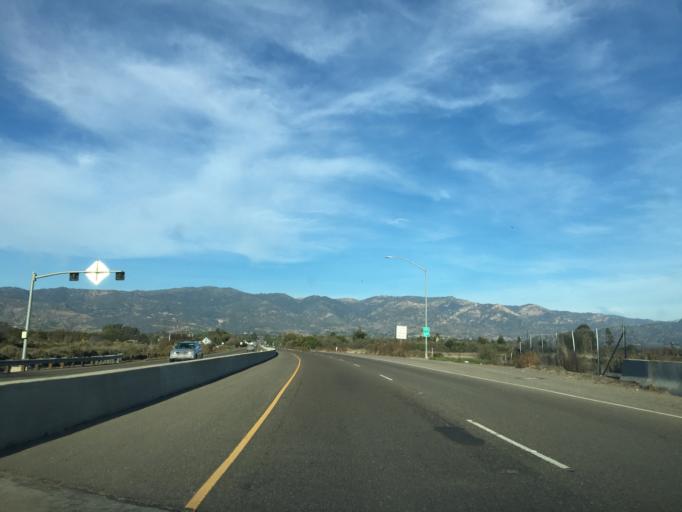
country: US
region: California
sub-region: Santa Barbara County
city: Goleta
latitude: 34.4210
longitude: -119.8297
